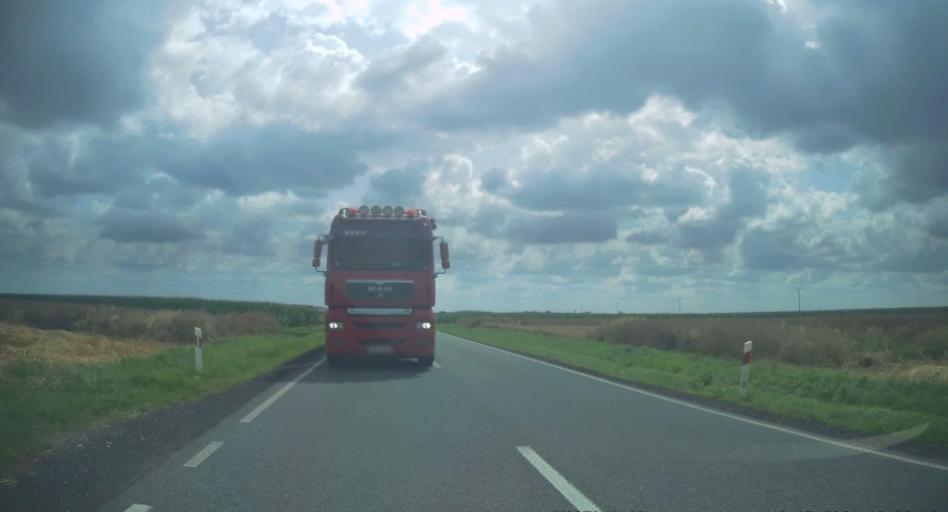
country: PL
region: Opole Voivodeship
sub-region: Powiat prudnicki
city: Glogowek
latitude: 50.3464
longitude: 17.8893
